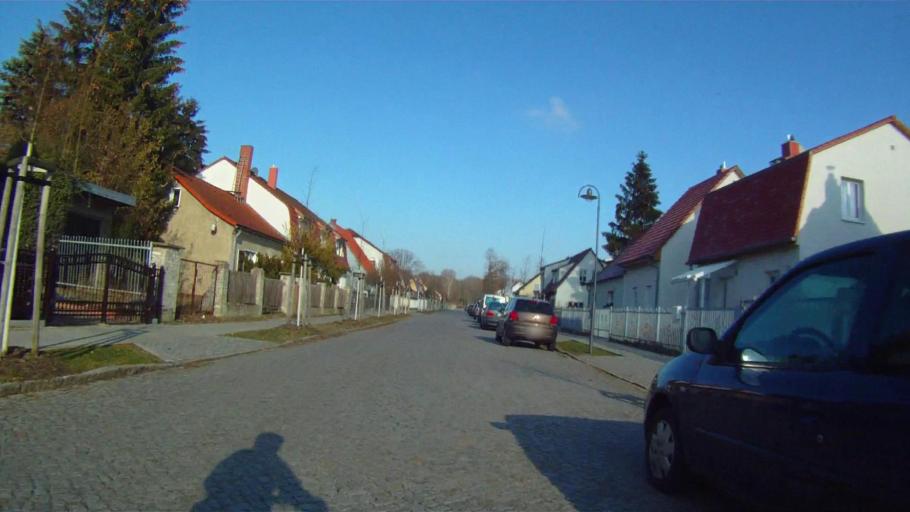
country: DE
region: Brandenburg
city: Erkner
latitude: 52.4328
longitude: 13.7510
